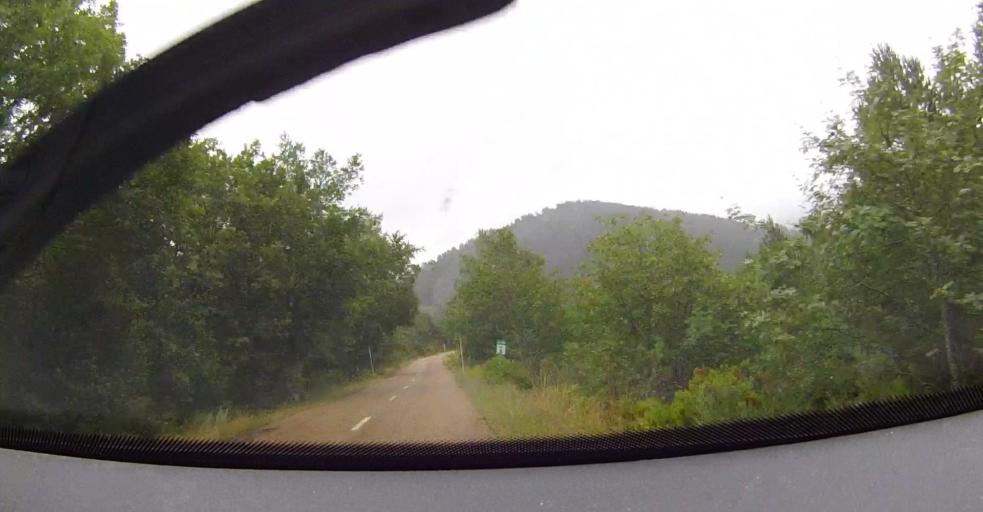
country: ES
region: Castille and Leon
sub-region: Provincia de Leon
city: Puebla de Lillo
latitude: 43.0674
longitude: -5.2682
